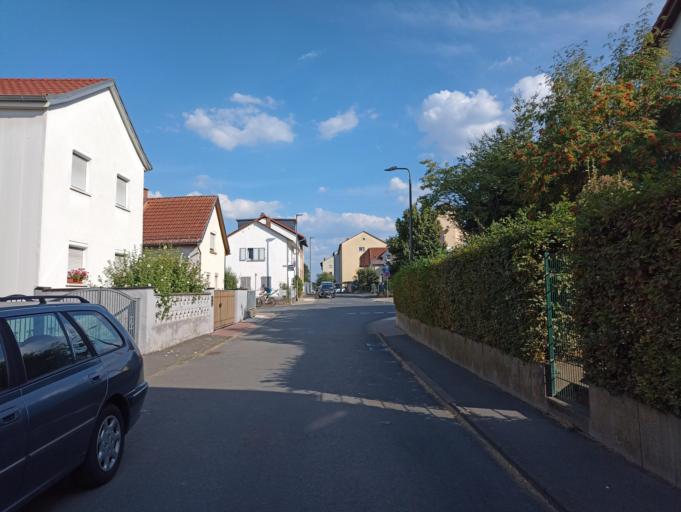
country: DE
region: Hesse
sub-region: Regierungsbezirk Darmstadt
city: Oberursel
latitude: 50.1976
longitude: 8.6030
